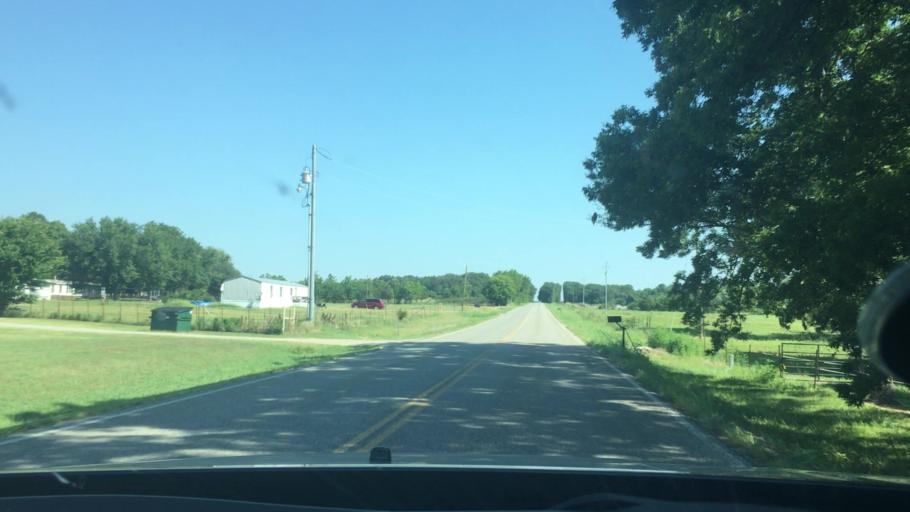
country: US
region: Oklahoma
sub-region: Johnston County
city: Tishomingo
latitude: 34.2900
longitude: -96.6185
